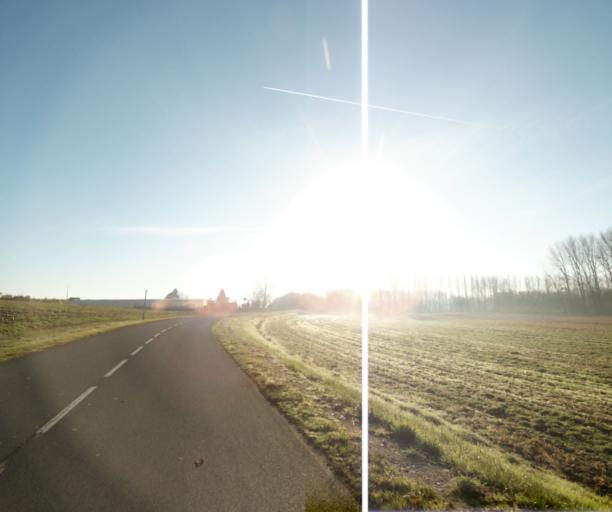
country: FR
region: Poitou-Charentes
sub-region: Departement de la Charente-Maritime
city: Cherac
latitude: 45.6962
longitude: -0.4807
